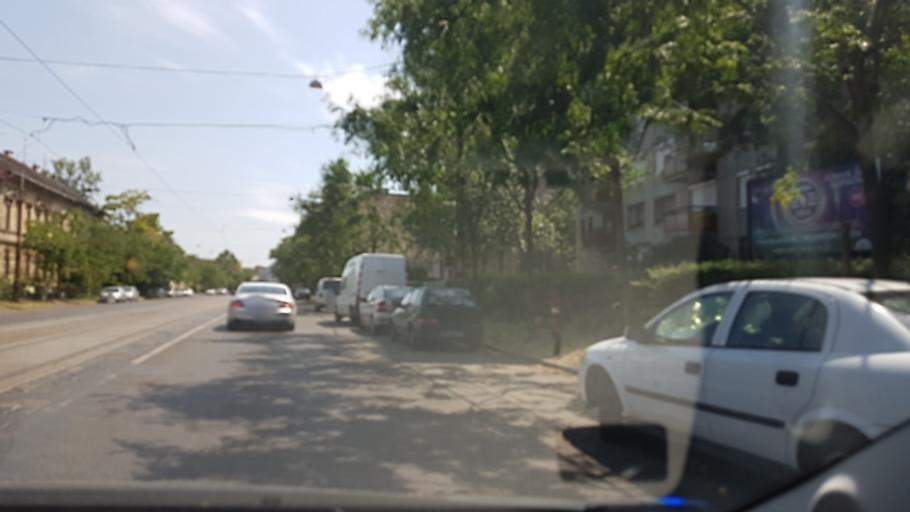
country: HU
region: Budapest
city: Budapest VIII. keruelet
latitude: 47.4844
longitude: 19.0930
